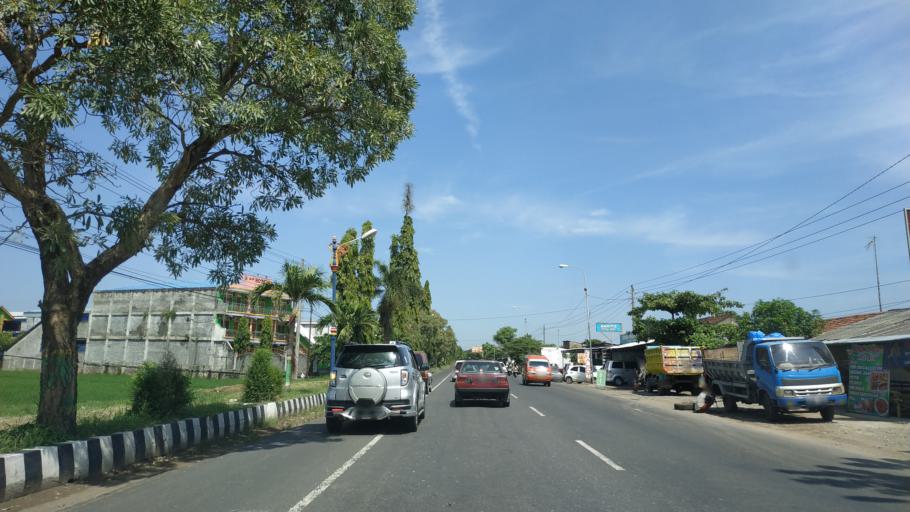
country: ID
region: Central Java
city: Geritan
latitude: -6.7497
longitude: 111.0581
